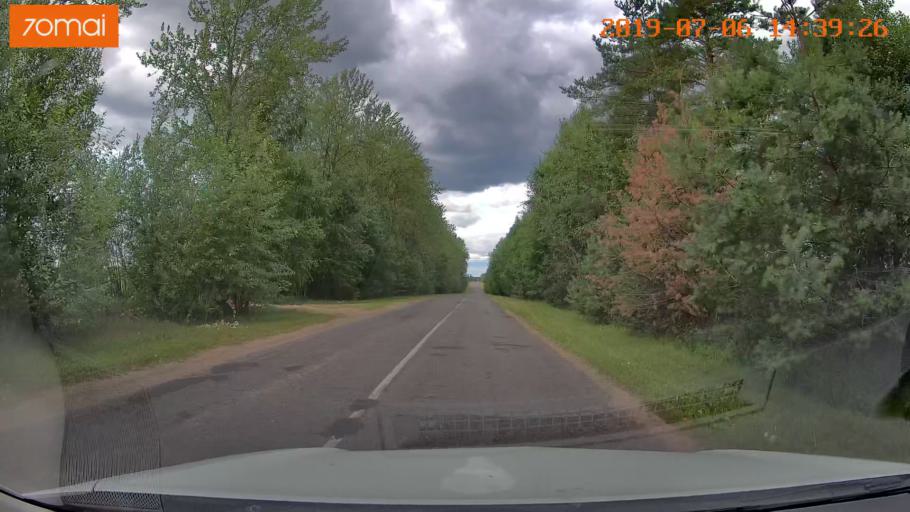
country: BY
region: Minsk
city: Ivyanyets
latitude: 53.9165
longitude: 26.6890
